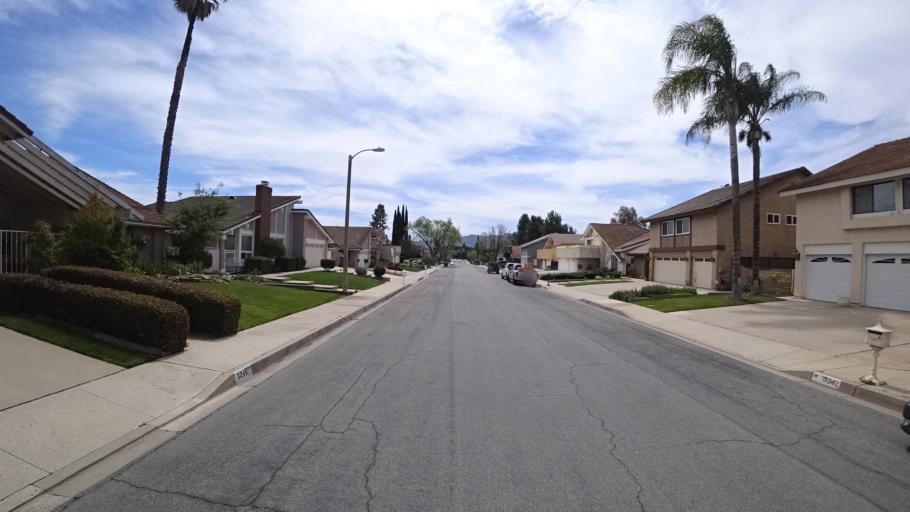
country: US
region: California
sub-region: Ventura County
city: Thousand Oaks
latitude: 34.1707
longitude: -118.8319
